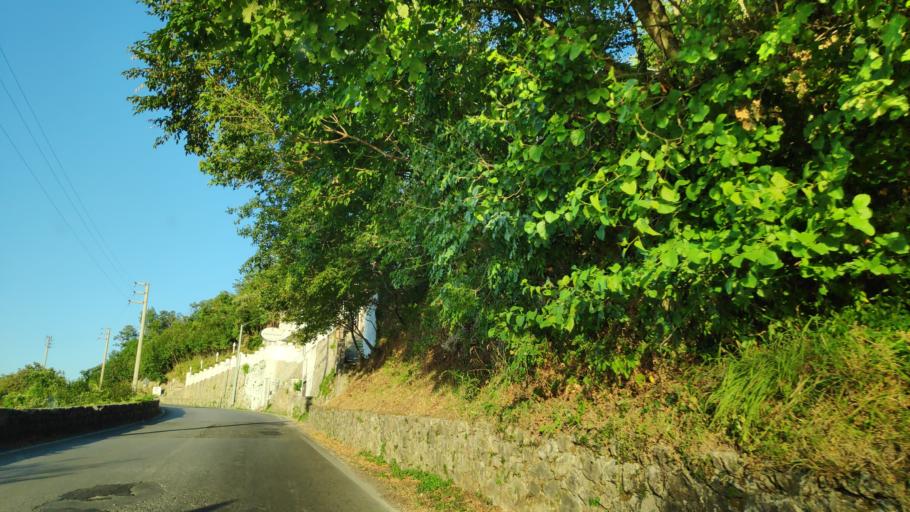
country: IT
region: Campania
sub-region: Provincia di Salerno
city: Corbara
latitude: 40.7247
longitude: 14.6027
